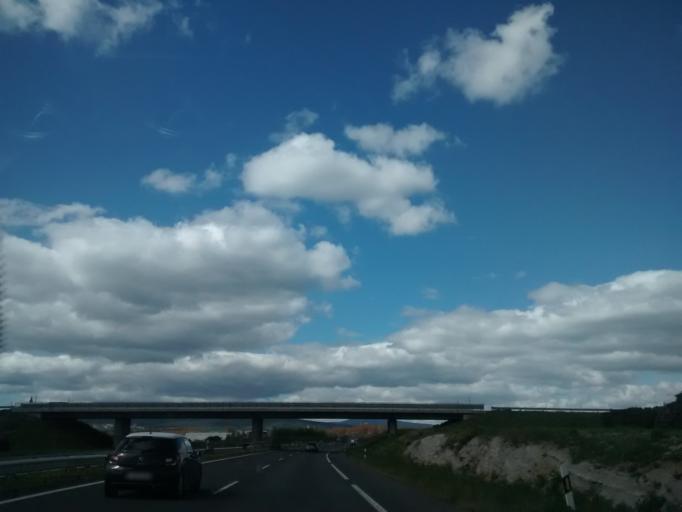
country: ES
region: Basque Country
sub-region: Provincia de Alava
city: Gasteiz / Vitoria
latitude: 42.8417
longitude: -2.7513
